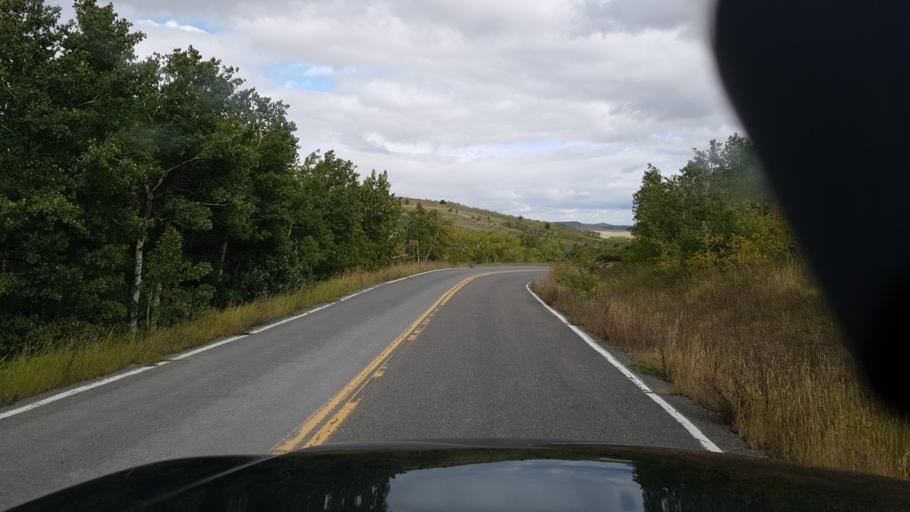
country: US
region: Montana
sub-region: Glacier County
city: South Browning
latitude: 48.5469
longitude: -113.2784
